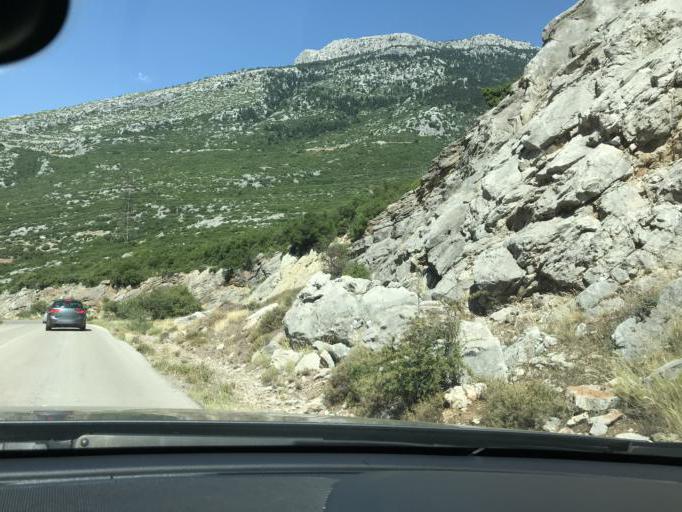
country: GR
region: Central Greece
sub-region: Nomos Voiotias
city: Distomo
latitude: 38.4922
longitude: 22.6959
